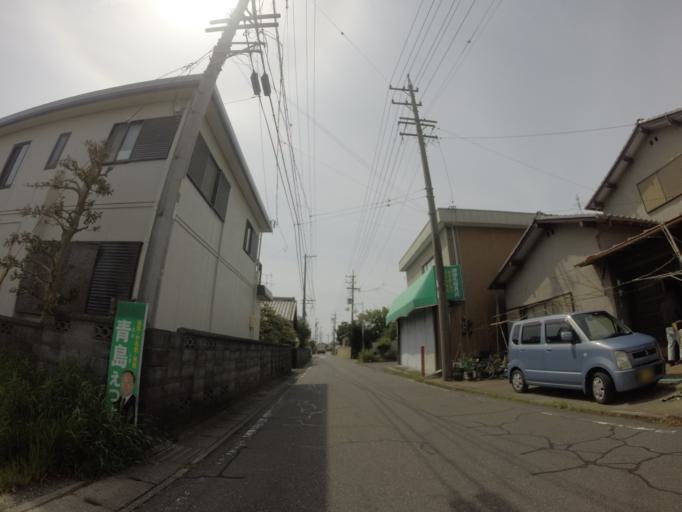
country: JP
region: Shizuoka
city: Fujieda
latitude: 34.8046
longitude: 138.2896
